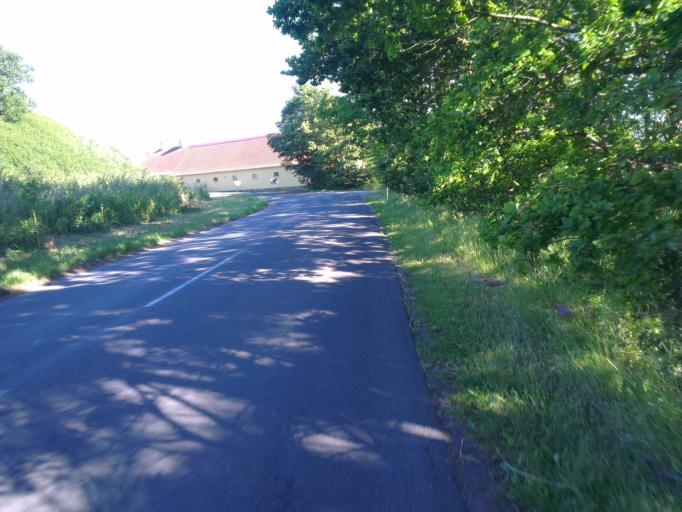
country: DK
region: Capital Region
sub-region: Frederikssund Kommune
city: Skibby
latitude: 55.7398
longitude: 11.9918
